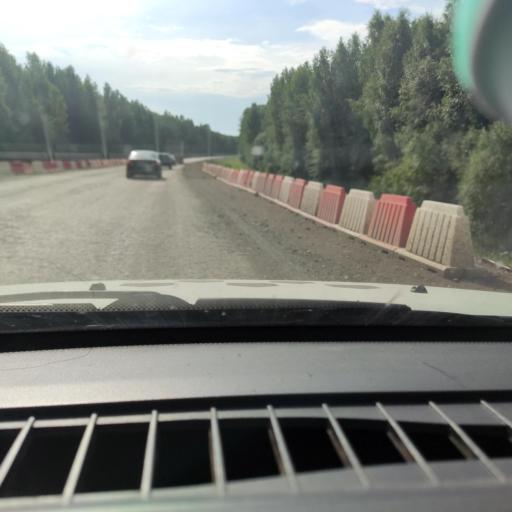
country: RU
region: Perm
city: Siva
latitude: 58.4801
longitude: 54.3969
